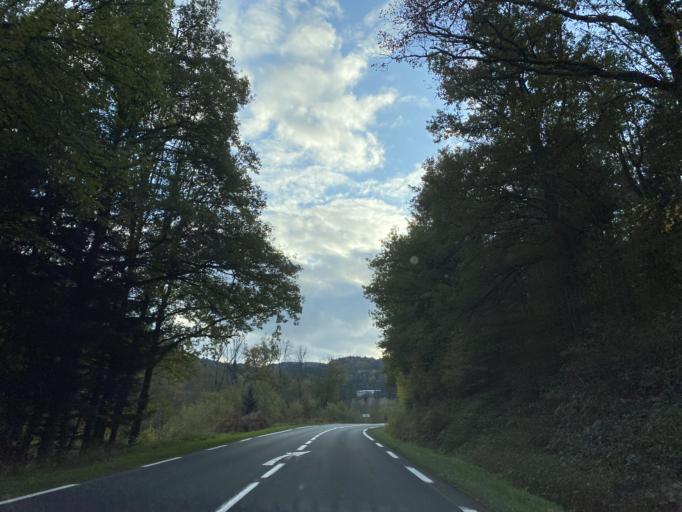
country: FR
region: Auvergne
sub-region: Departement du Puy-de-Dome
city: Job
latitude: 45.6478
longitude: 3.6731
